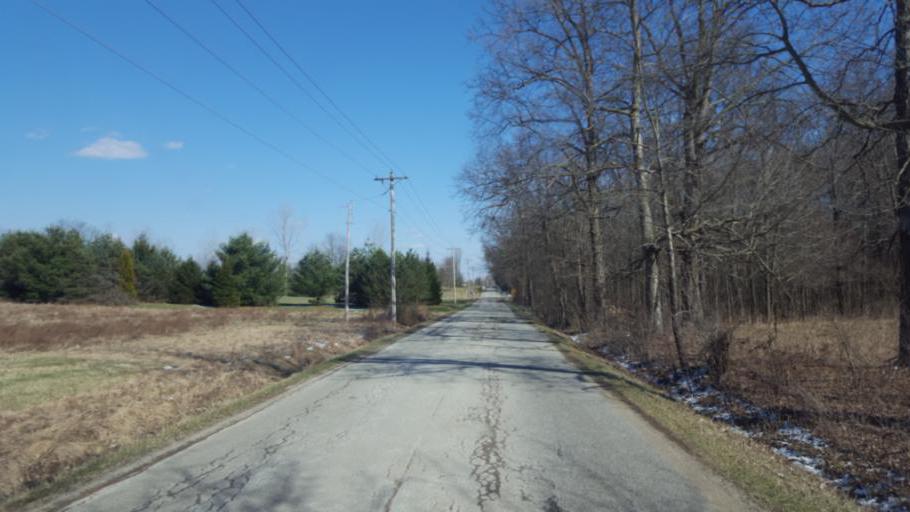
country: US
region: Ohio
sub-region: Knox County
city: Fredericktown
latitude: 40.4325
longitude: -82.6618
